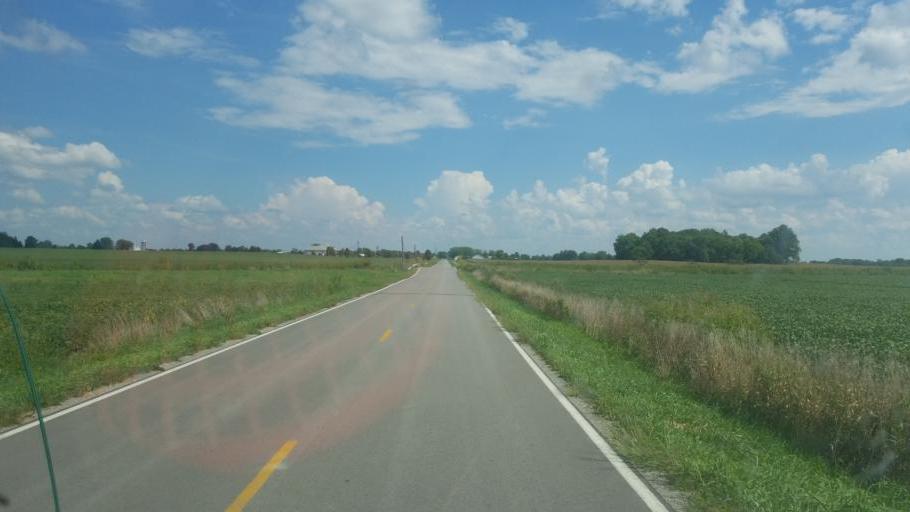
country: US
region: Ohio
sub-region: Hardin County
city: Forest
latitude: 40.8615
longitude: -83.4873
